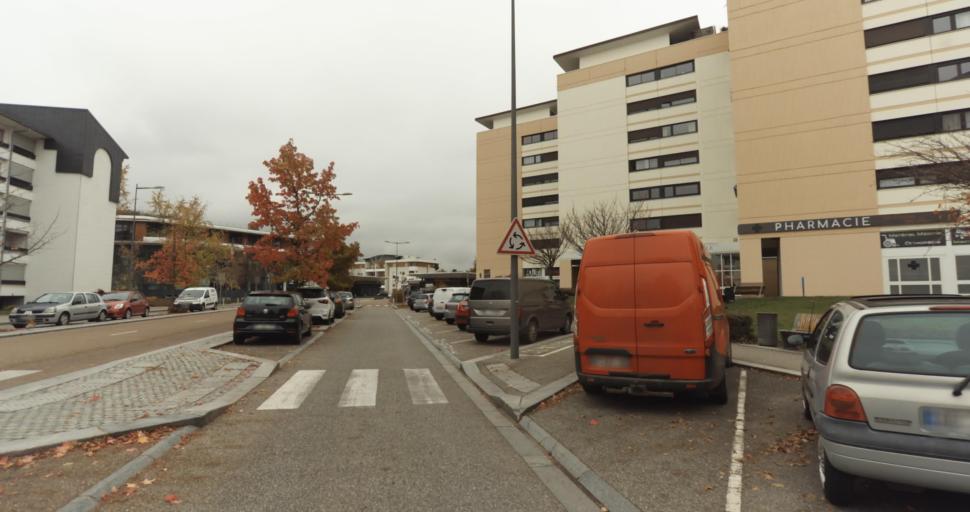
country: FR
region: Rhone-Alpes
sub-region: Departement de la Haute-Savoie
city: Cran-Gevrier
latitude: 45.8900
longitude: 6.1013
